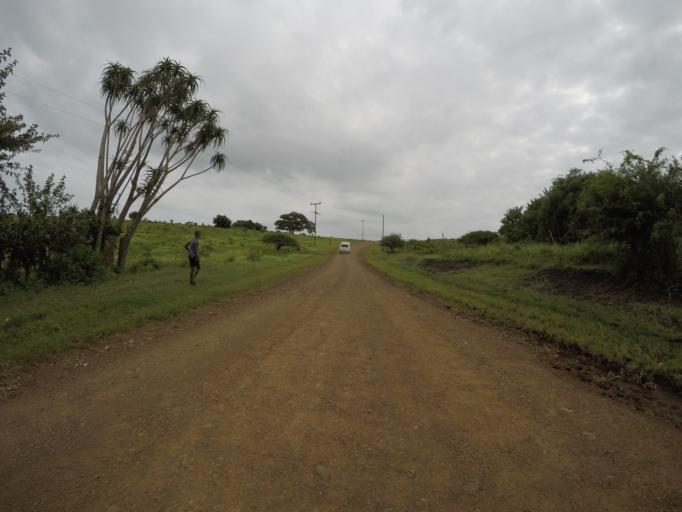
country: ZA
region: KwaZulu-Natal
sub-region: uThungulu District Municipality
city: Empangeni
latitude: -28.6381
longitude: 31.9049
